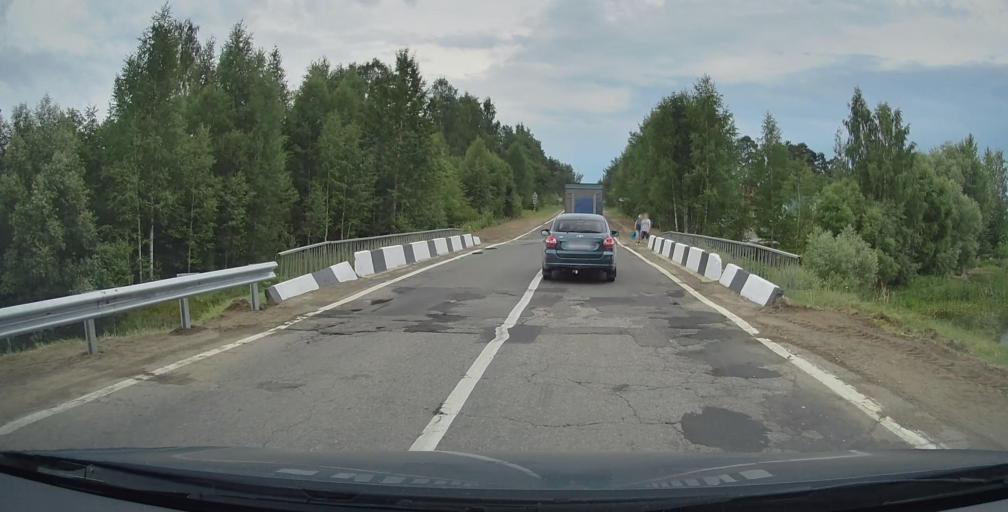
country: RU
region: Jaroslavl
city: Myshkin
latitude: 57.8554
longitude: 38.5098
